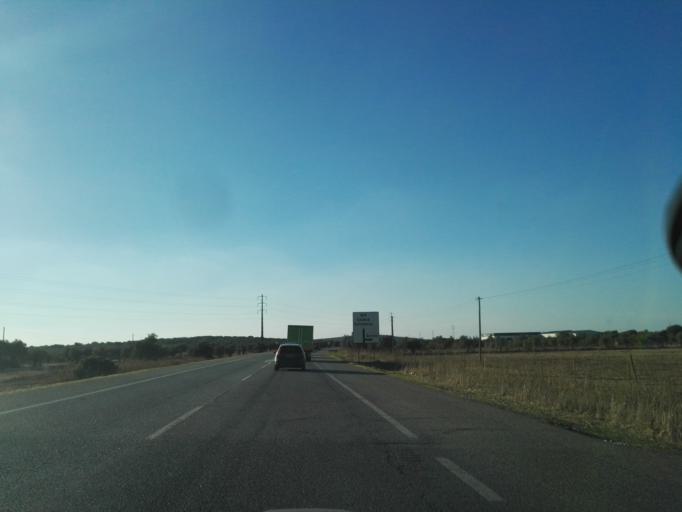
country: PT
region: Evora
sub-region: Borba
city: Borba
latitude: 38.8208
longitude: -7.4943
